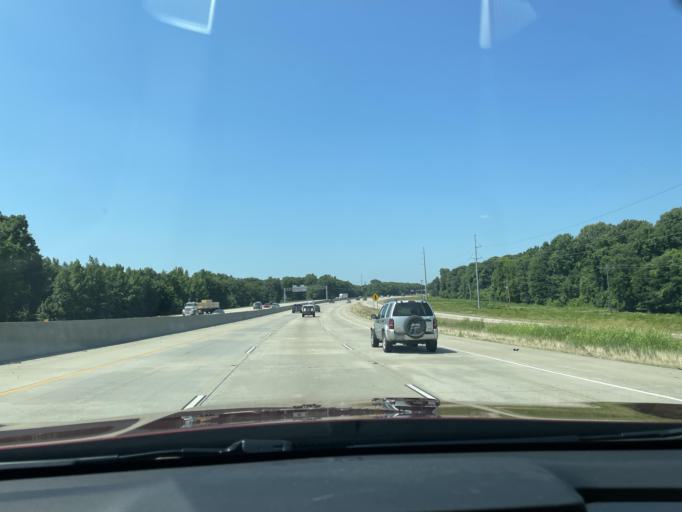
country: US
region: Arkansas
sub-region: Pulaski County
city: Jacksonville
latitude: 34.8597
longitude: -92.1310
